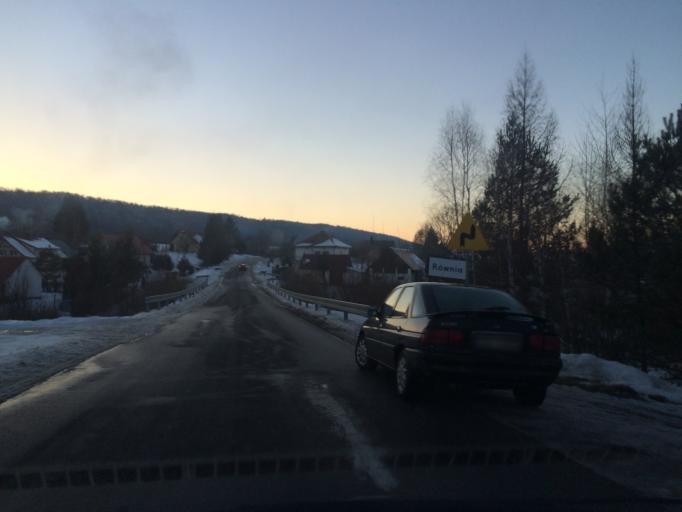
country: PL
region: Subcarpathian Voivodeship
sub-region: Powiat bieszczadzki
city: Ustrzyki Dolne
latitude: 49.4004
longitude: 22.6002
